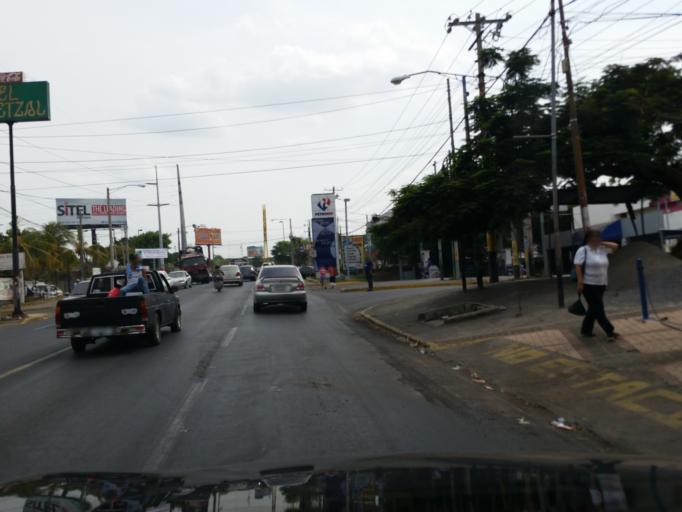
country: NI
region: Managua
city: Managua
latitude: 12.1147
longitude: -86.2541
